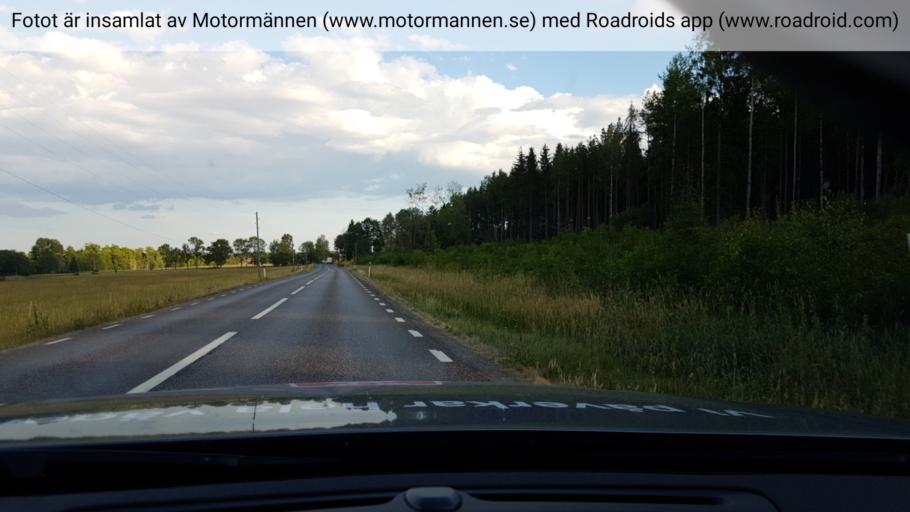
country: SE
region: Uppsala
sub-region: Enkopings Kommun
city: Irsta
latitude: 59.7754
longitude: 16.9097
